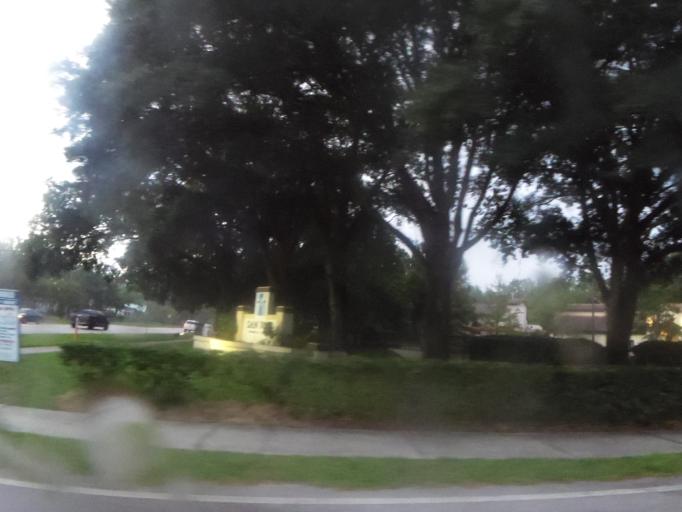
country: US
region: Florida
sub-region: Duval County
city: Jacksonville
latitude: 30.2473
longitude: -81.6256
